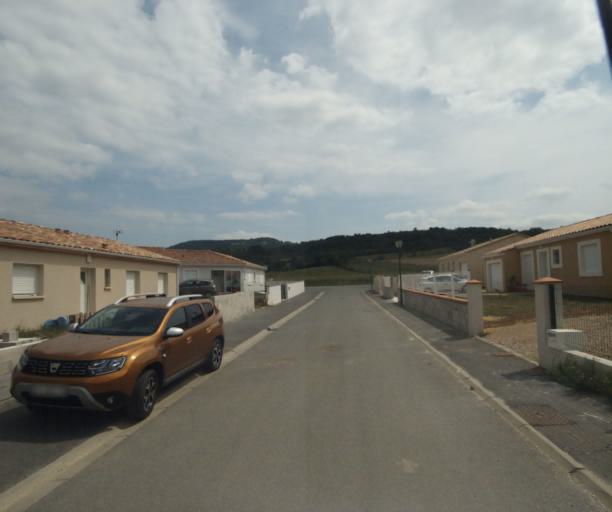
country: FR
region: Midi-Pyrenees
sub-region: Departement du Tarn
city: Soreze
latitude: 43.4505
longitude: 2.0385
